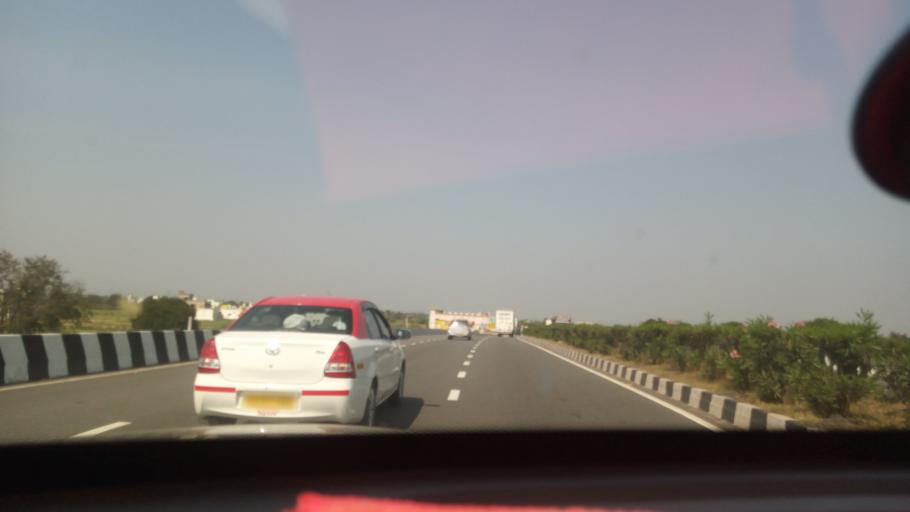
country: IN
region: Tamil Nadu
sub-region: Dharmapuri
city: Dharmapuri
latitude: 12.1411
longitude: 78.1408
